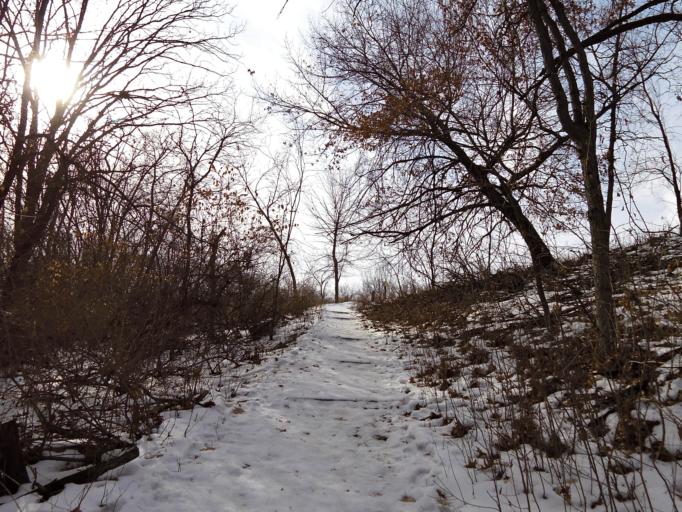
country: US
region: Minnesota
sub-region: Hennepin County
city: Richfield
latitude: 44.8590
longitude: -93.2145
